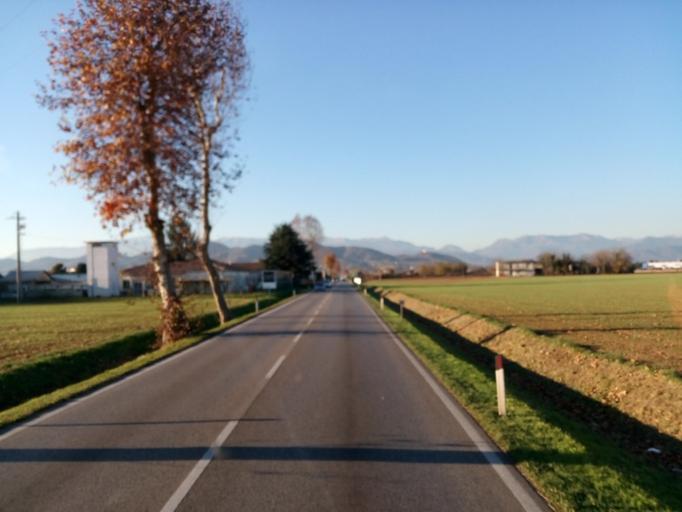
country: IT
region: Veneto
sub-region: Provincia di Treviso
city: Crocetta-Nogare
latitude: 45.8046
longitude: 12.0275
